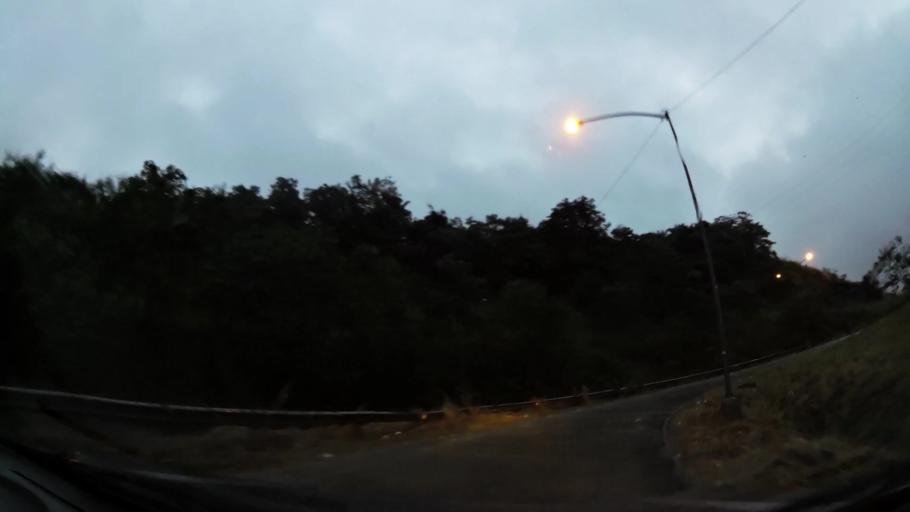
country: PA
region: Panama
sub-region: Distrito de Panama
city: Paraiso
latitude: 9.0374
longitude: -79.6308
